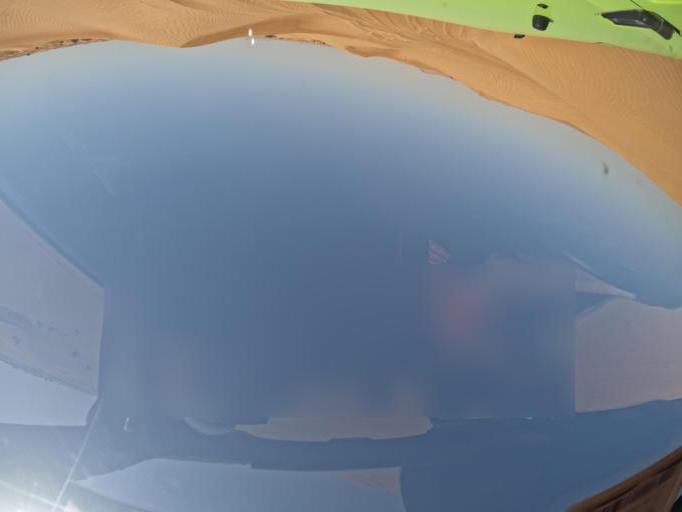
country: AE
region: Ash Shariqah
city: Adh Dhayd
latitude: 24.9619
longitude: 55.7204
